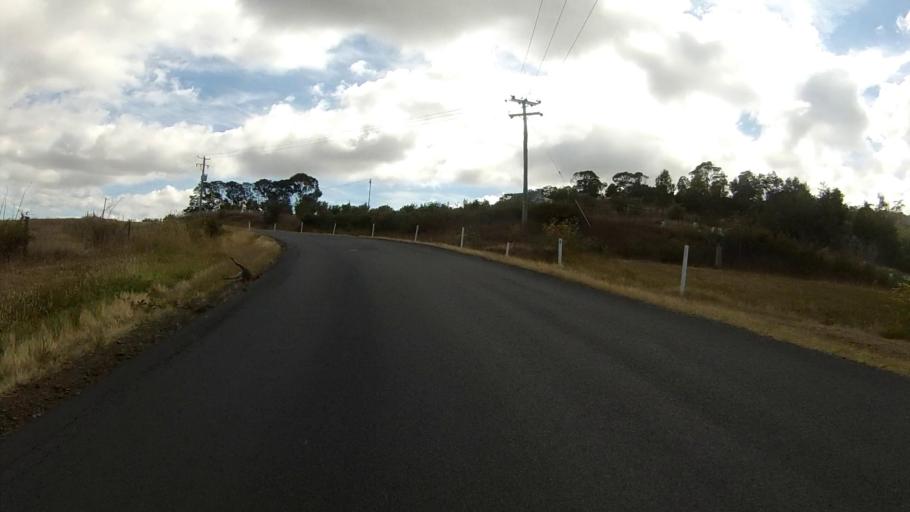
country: AU
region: Tasmania
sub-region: Brighton
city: Old Beach
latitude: -42.7589
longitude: 147.3042
